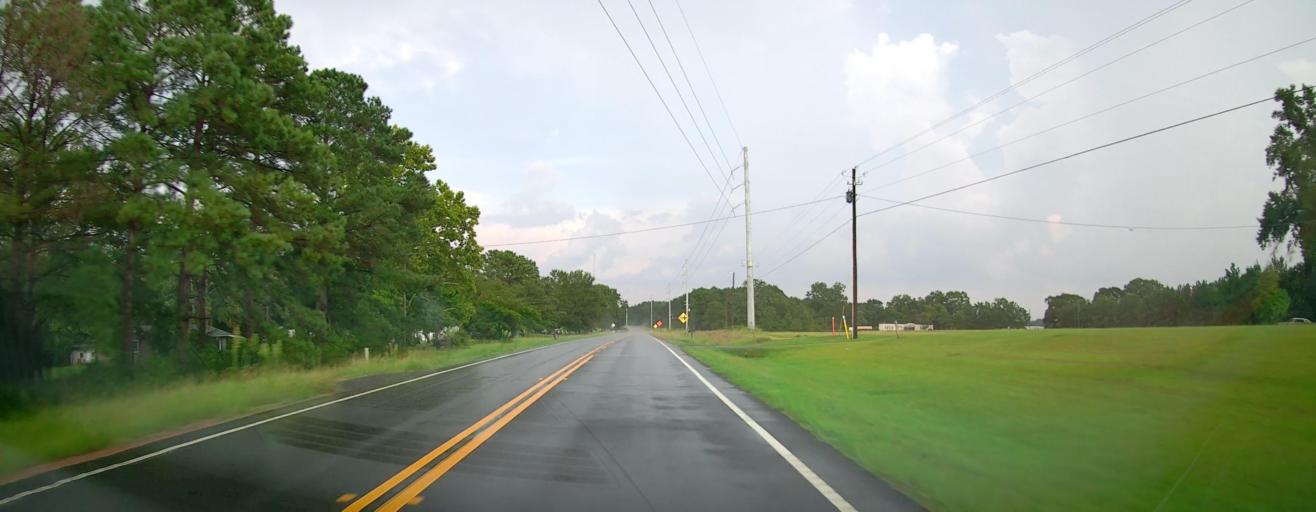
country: US
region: Georgia
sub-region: Twiggs County
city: Jeffersonville
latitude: 32.5764
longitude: -83.2046
